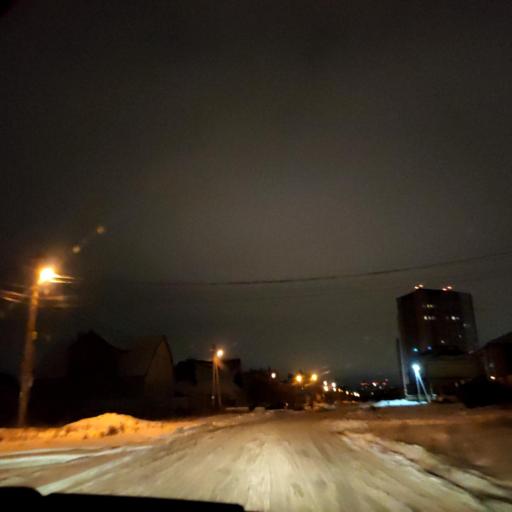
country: RU
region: Voronezj
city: Podgornoye
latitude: 51.7246
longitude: 39.1383
